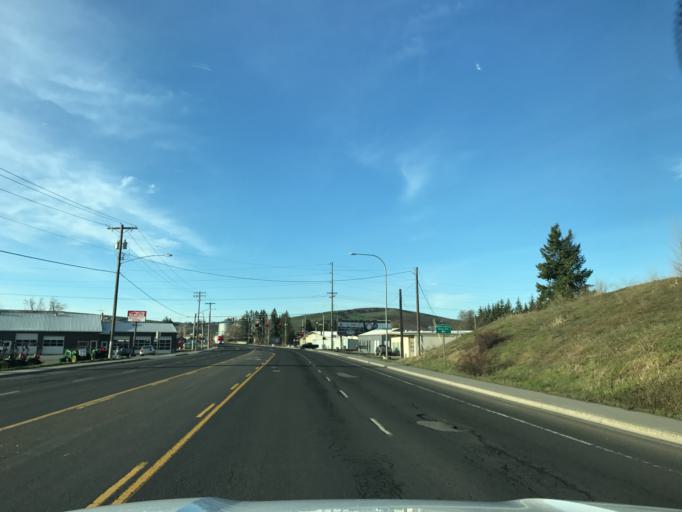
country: US
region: Idaho
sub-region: Latah County
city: Moscow
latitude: 46.7171
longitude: -117.0027
